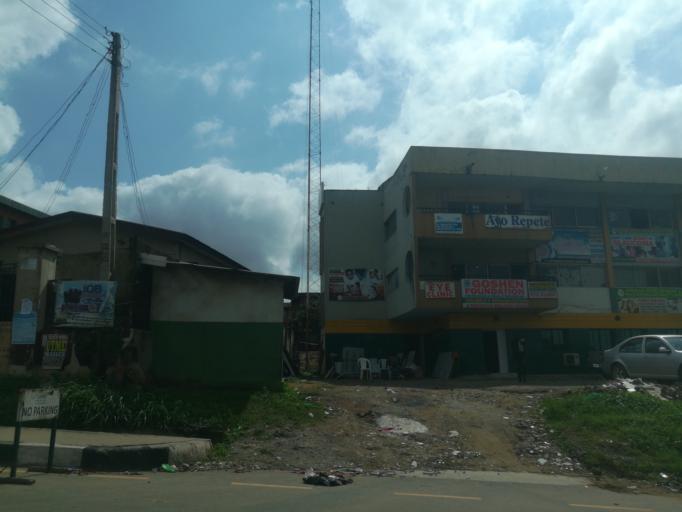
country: NG
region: Oyo
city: Ibadan
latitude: 7.3386
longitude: 3.8706
